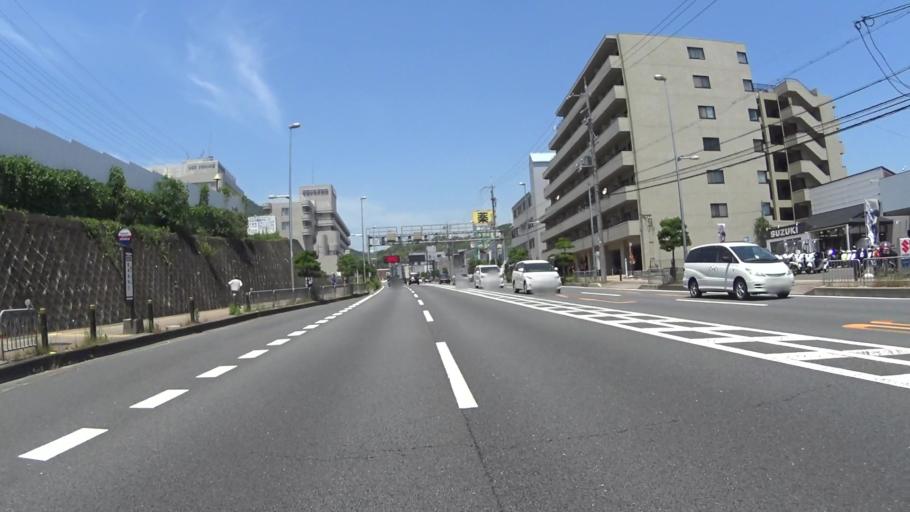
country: JP
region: Kyoto
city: Muko
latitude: 34.9734
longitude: 135.6694
